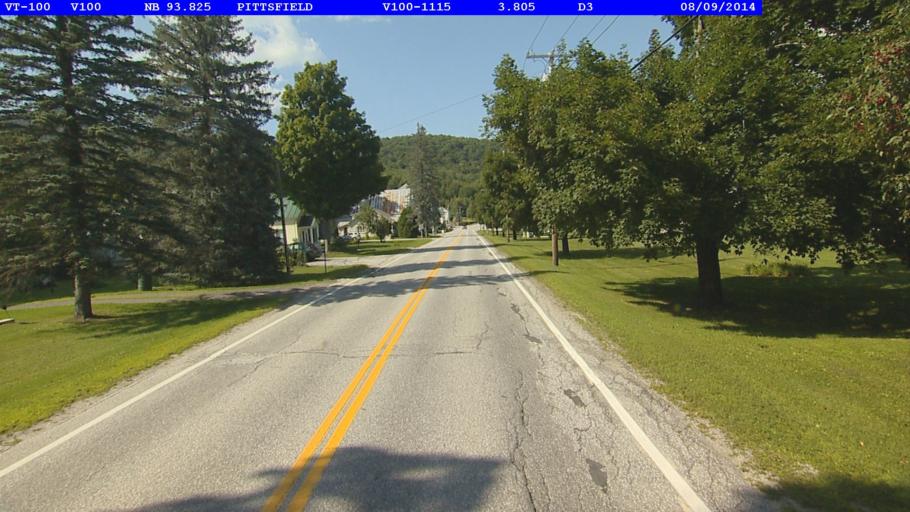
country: US
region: Vermont
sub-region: Orange County
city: Randolph
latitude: 43.7704
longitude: -72.8129
